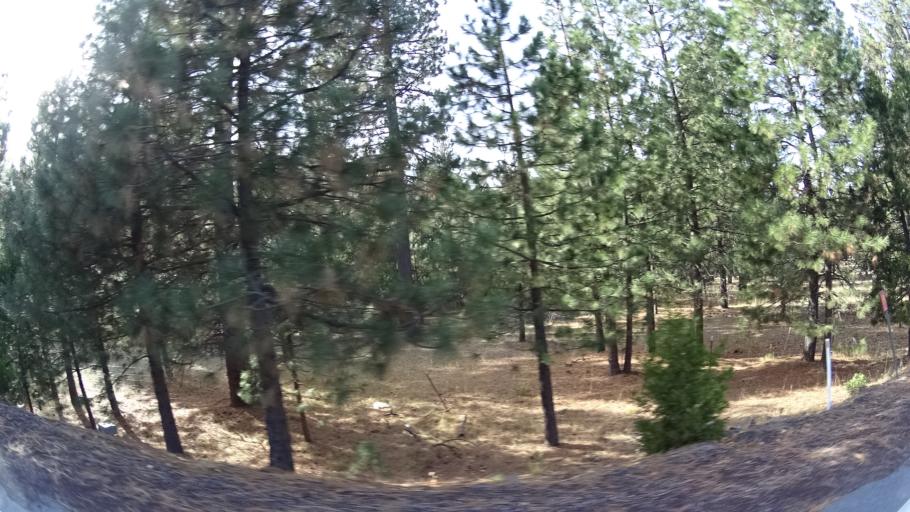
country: US
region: California
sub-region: Siskiyou County
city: Weed
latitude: 41.3924
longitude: -122.4129
